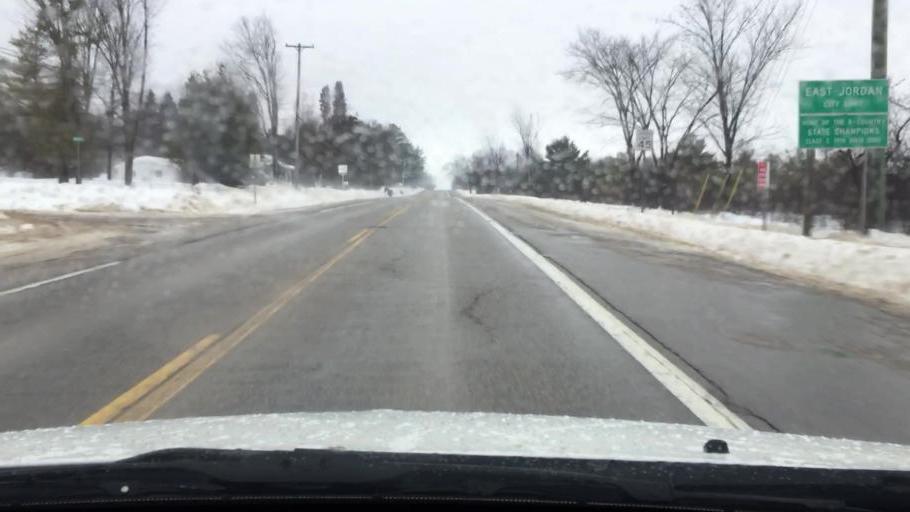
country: US
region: Michigan
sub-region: Charlevoix County
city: East Jordan
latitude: 45.1397
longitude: -85.1397
